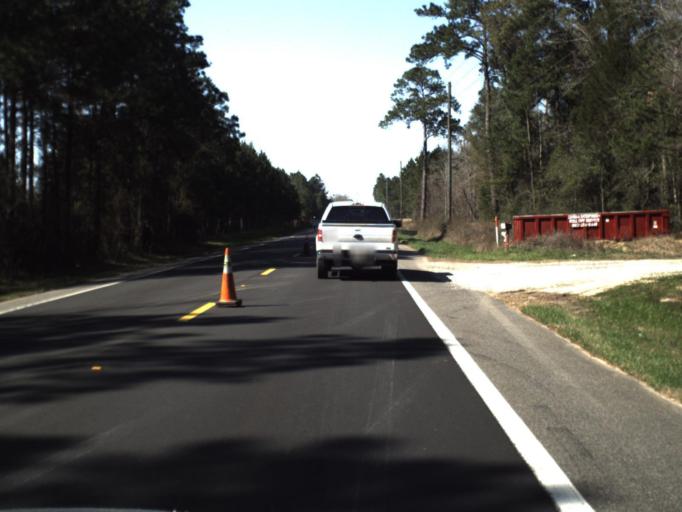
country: US
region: Florida
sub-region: Jackson County
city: Marianna
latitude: 30.6854
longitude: -85.1765
